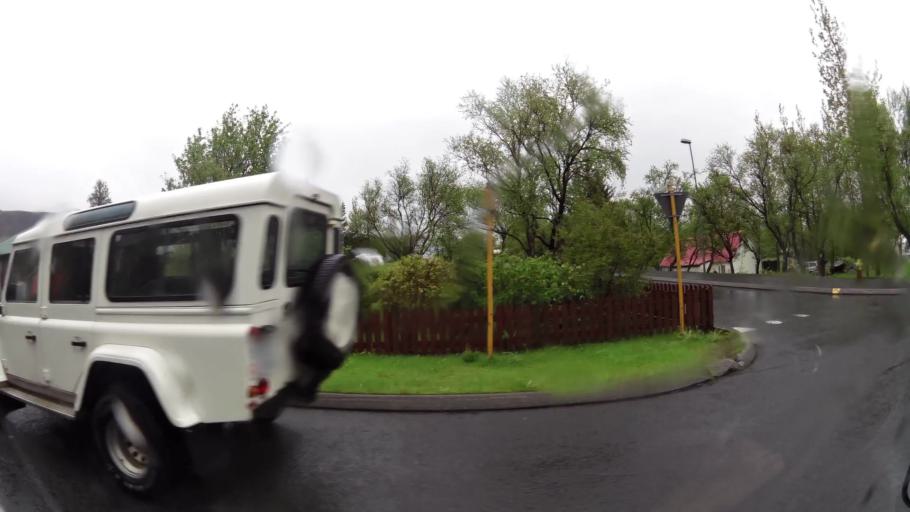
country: IS
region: South
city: Hveragerdi
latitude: 64.0049
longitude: -21.1897
